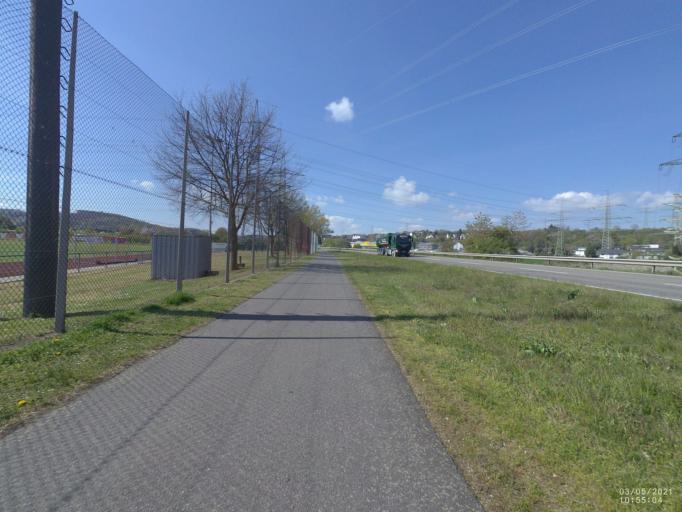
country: DE
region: Rheinland-Pfalz
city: Kettig
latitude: 50.4032
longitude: 7.4674
